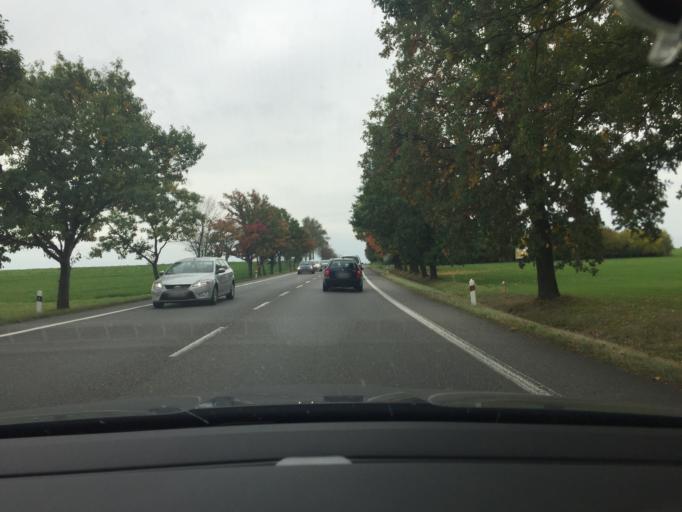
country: CZ
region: Jihocesky
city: Cimelice
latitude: 49.4601
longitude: 14.0678
